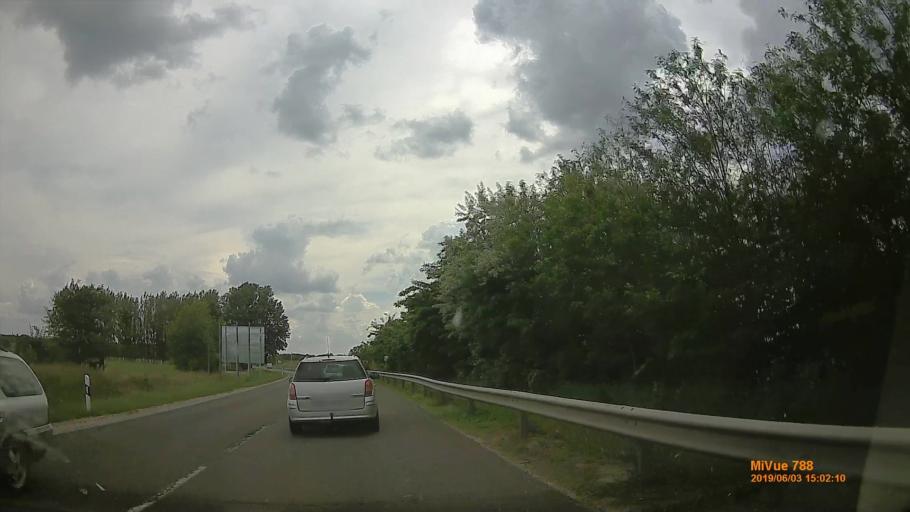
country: HU
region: Bacs-Kiskun
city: Helvecia
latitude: 46.8470
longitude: 19.6588
